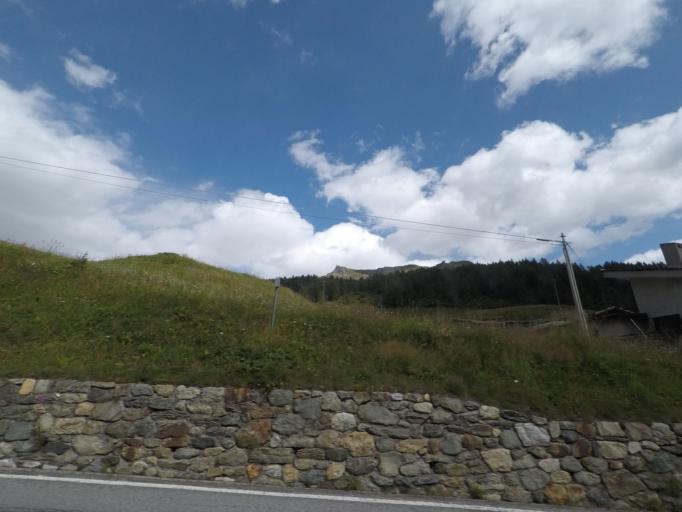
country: IT
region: Aosta Valley
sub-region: Valle d'Aosta
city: Paquier
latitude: 45.9207
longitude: 7.6169
